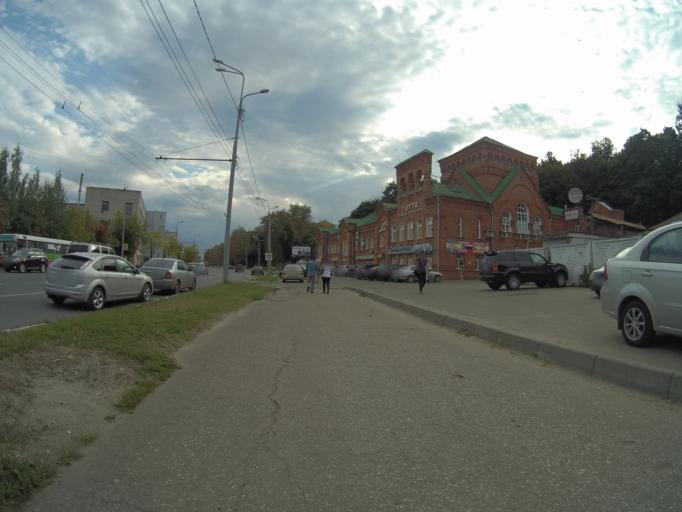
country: RU
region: Vladimir
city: Kommunar
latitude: 56.1420
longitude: 40.4375
